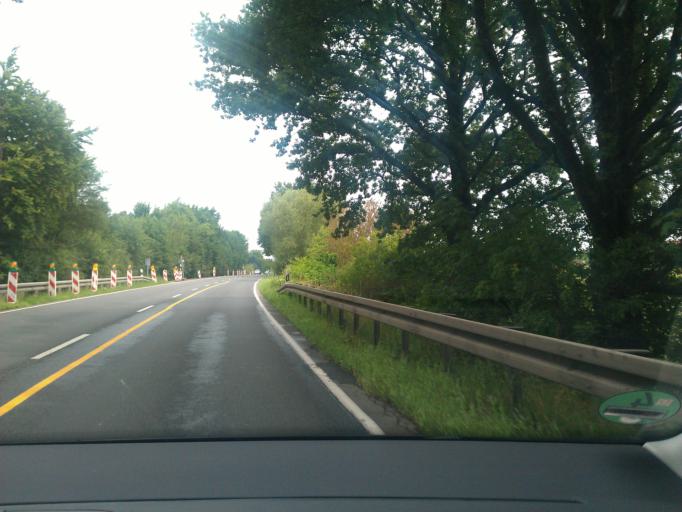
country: BE
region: Wallonia
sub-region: Province de Liege
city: Raeren
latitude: 50.7076
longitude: 6.1415
